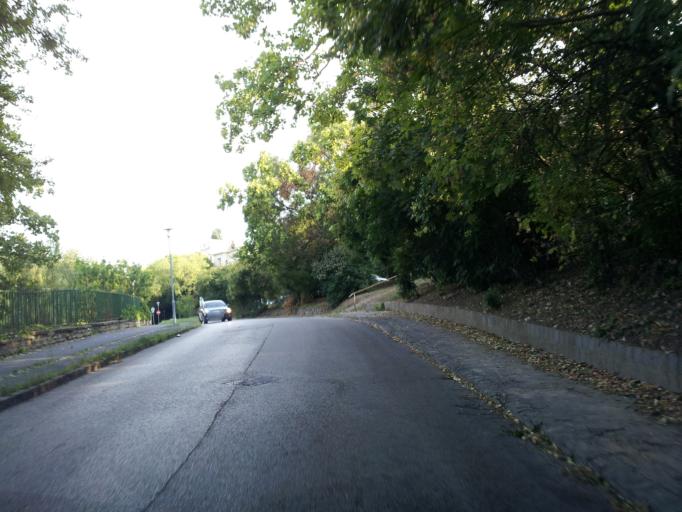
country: HU
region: Budapest
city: Budapest XII. keruelet
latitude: 47.5020
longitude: 19.0182
